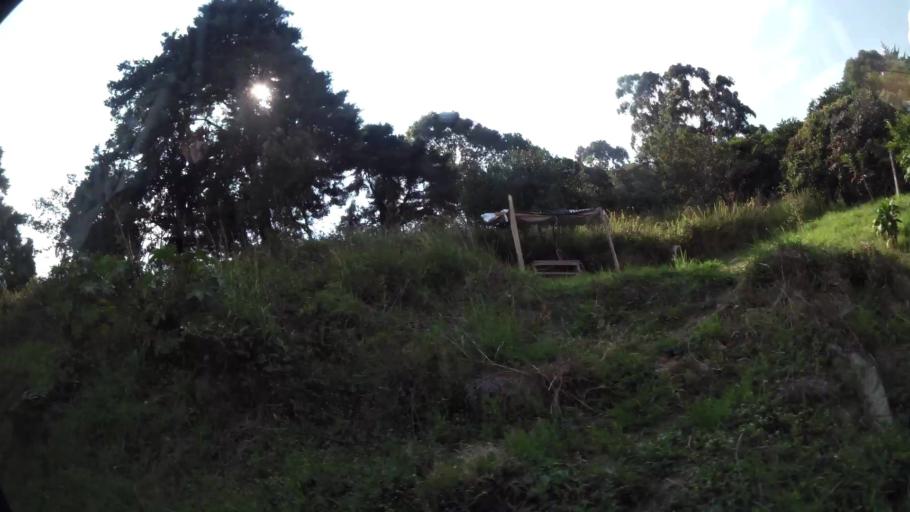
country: CO
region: Antioquia
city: Medellin
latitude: 6.2925
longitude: -75.5955
